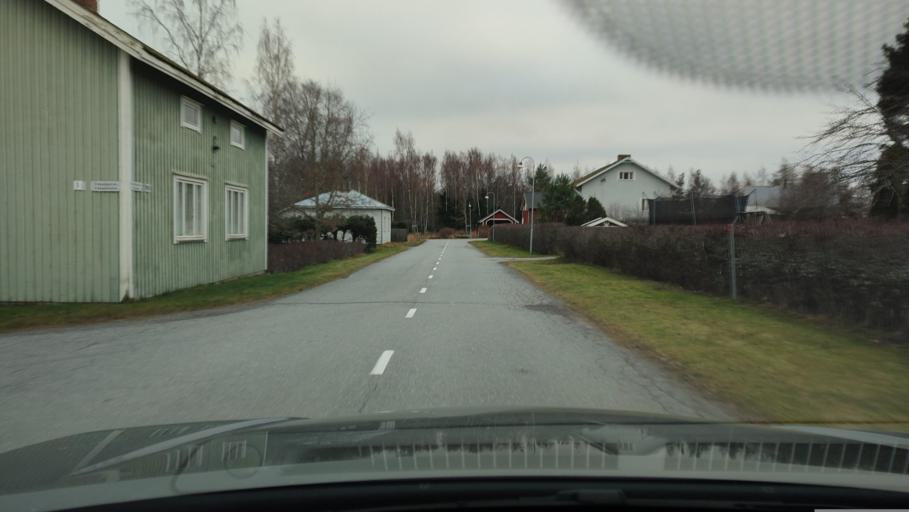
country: FI
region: Ostrobothnia
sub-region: Sydosterbotten
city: Kristinestad
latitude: 62.2673
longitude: 21.3725
